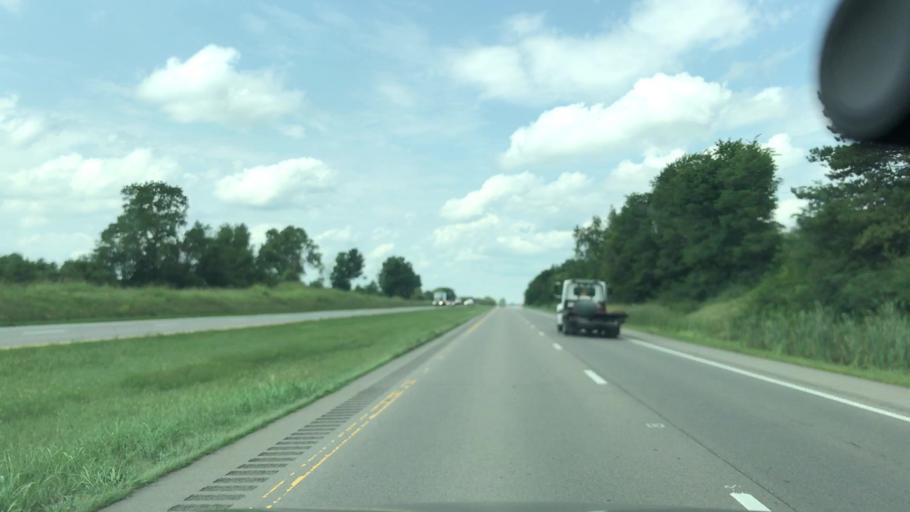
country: US
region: Ohio
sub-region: Ross County
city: Kingston
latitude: 39.4686
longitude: -82.9702
